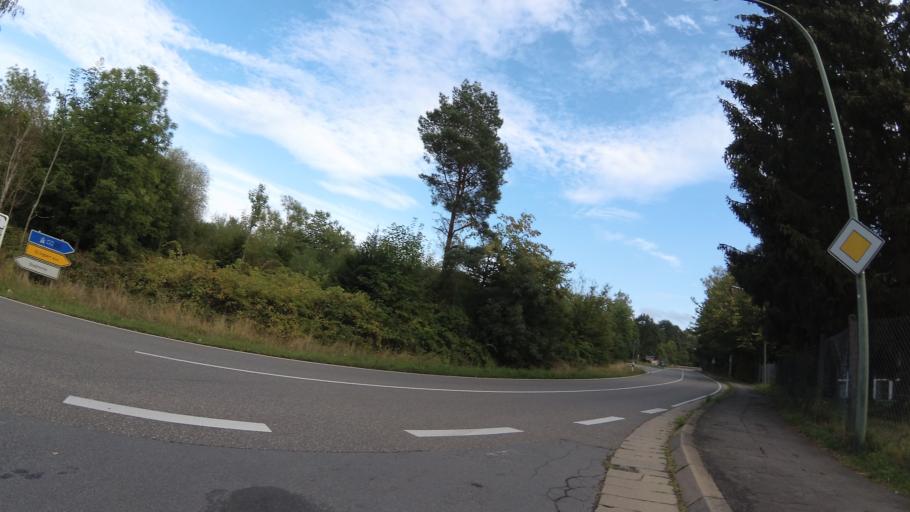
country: DE
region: Saarland
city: Sulzbach
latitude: 49.2884
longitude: 7.0765
